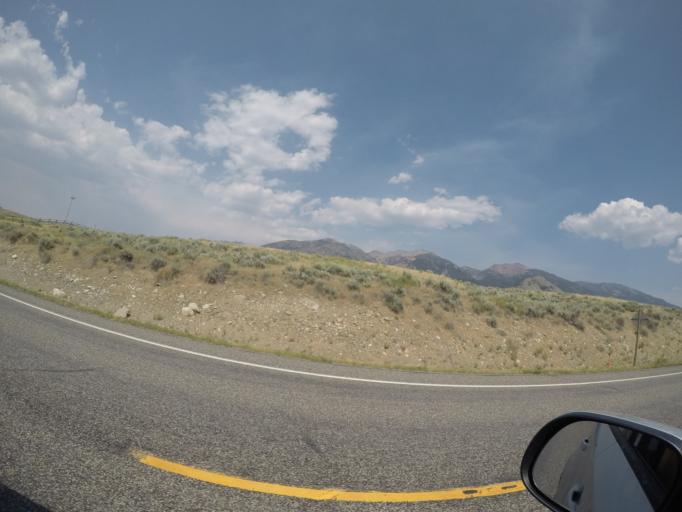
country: US
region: Montana
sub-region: Gallatin County
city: Big Sky
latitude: 44.8518
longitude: -111.5368
